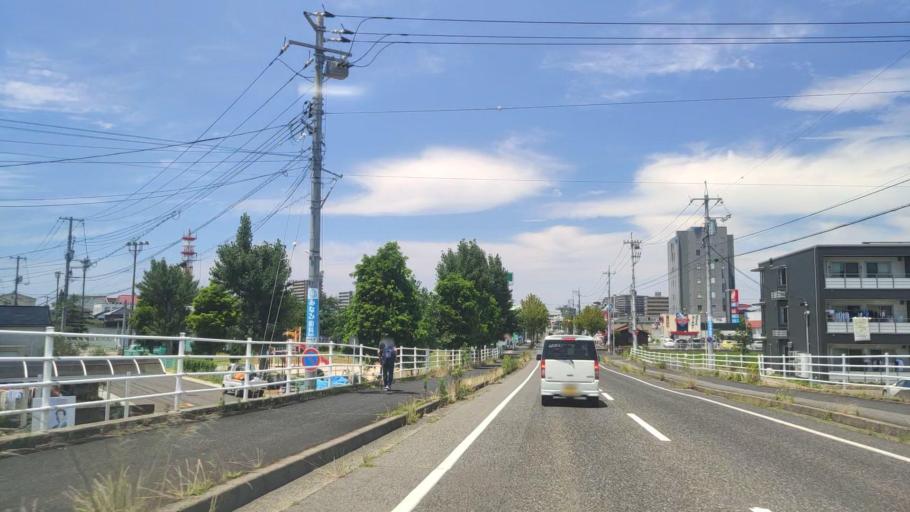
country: JP
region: Tottori
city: Tottori
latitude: 35.4847
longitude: 134.2338
